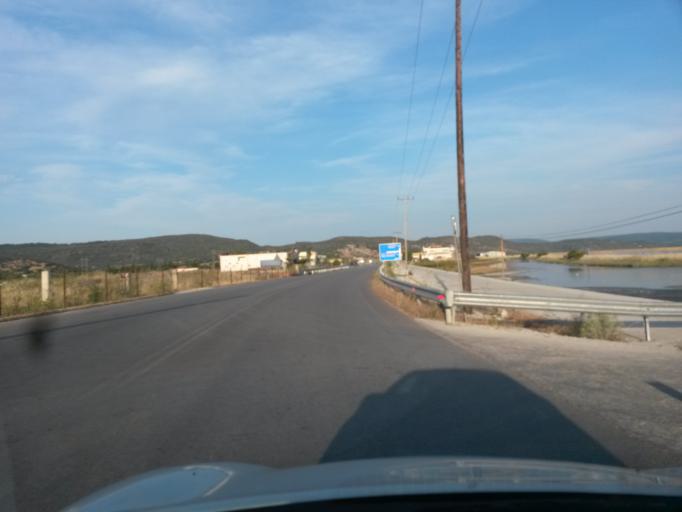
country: GR
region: North Aegean
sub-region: Nomos Lesvou
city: Kalloni
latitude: 39.2258
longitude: 26.2426
